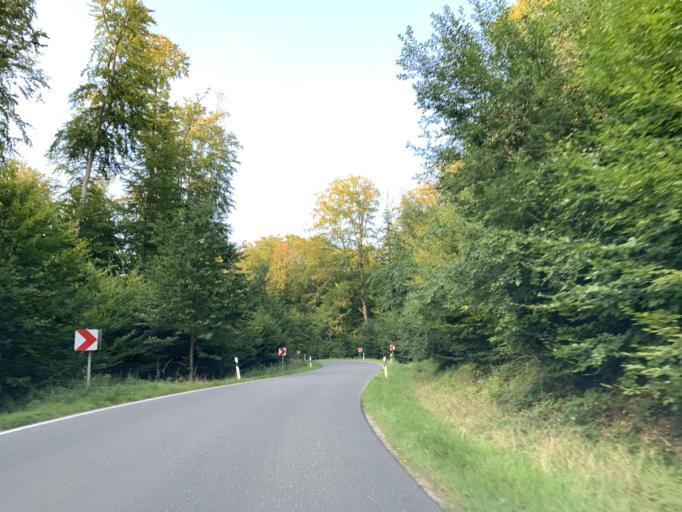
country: DE
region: Mecklenburg-Vorpommern
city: Loitz
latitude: 53.3481
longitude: 13.4300
